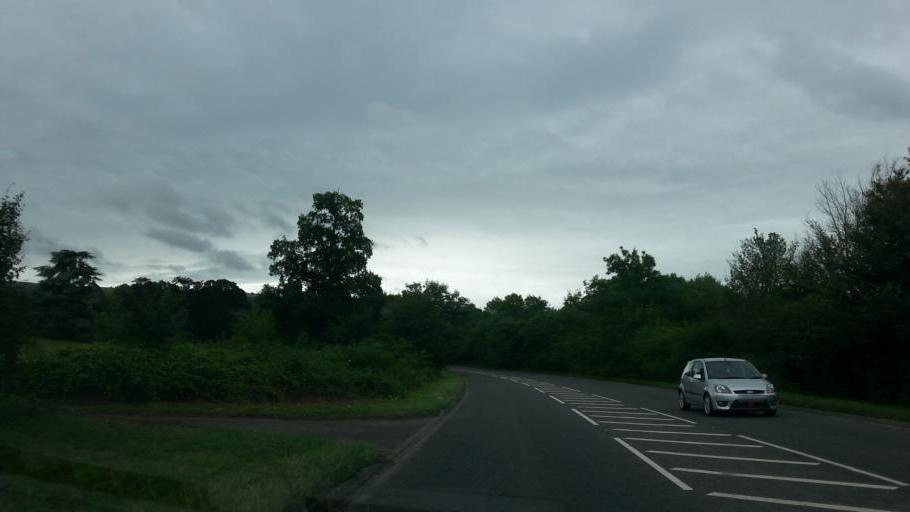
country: GB
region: England
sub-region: Wiltshire
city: Westbury
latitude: 51.2810
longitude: -2.1837
